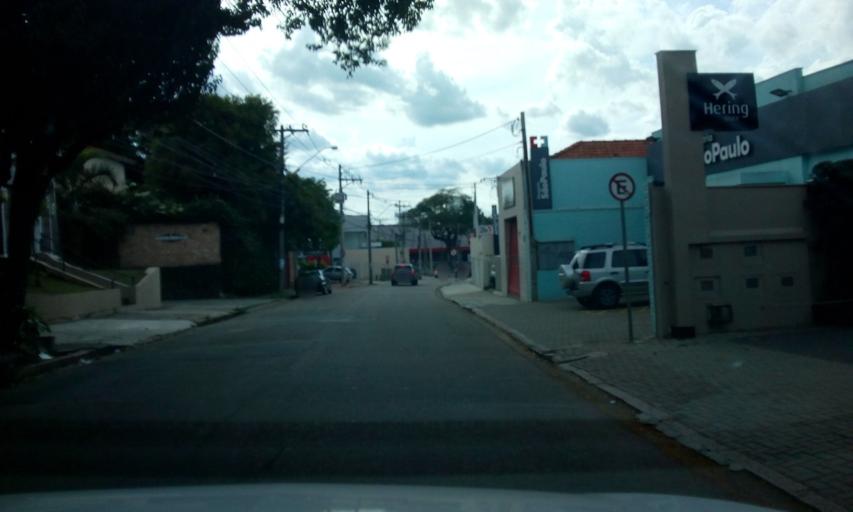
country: BR
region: Sao Paulo
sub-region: Jundiai
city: Jundiai
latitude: -23.1877
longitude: -46.8961
